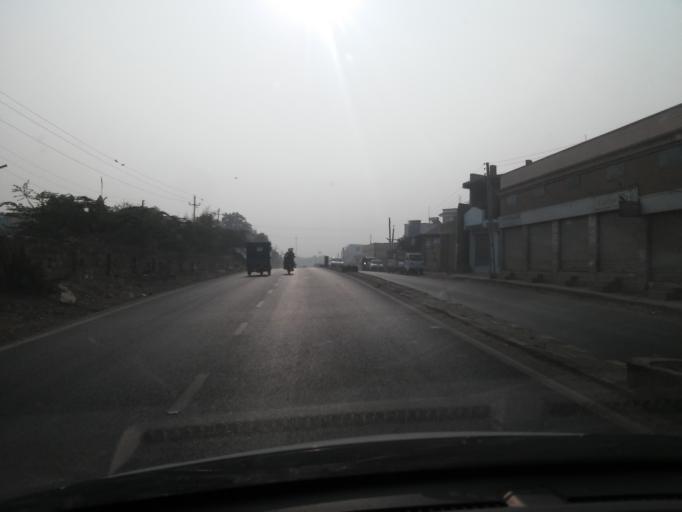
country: IN
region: Gujarat
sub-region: Kachchh
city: Bhuj
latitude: 23.2421
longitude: 69.7089
